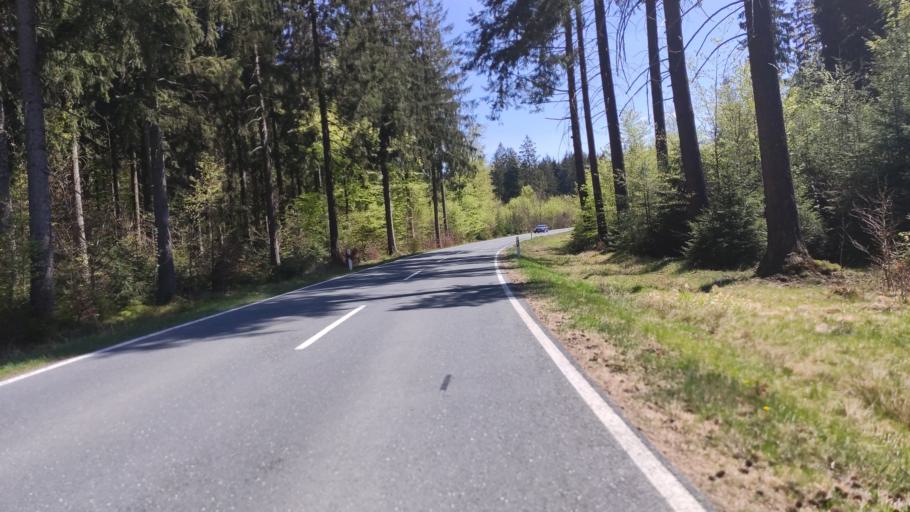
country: DE
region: Bavaria
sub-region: Upper Franconia
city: Tschirn
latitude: 50.3635
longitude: 11.4632
